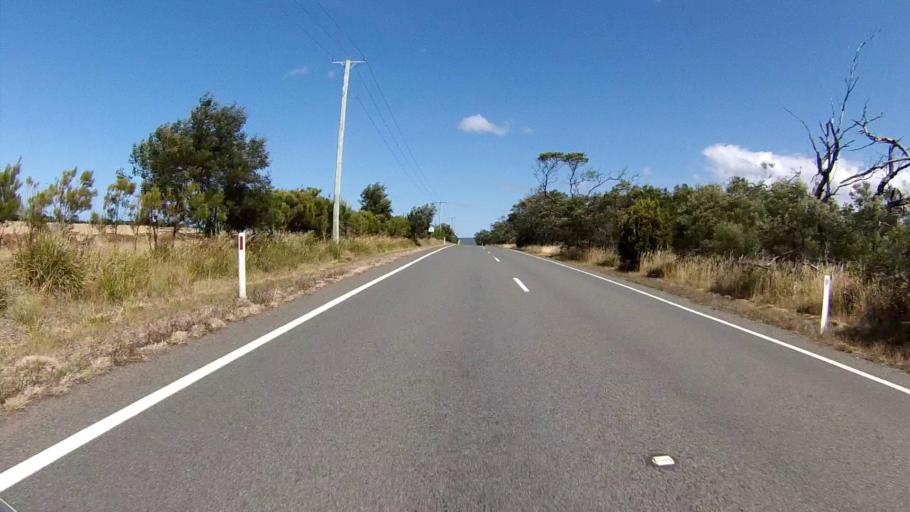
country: AU
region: Tasmania
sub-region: Break O'Day
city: St Helens
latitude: -42.0938
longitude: 148.0649
